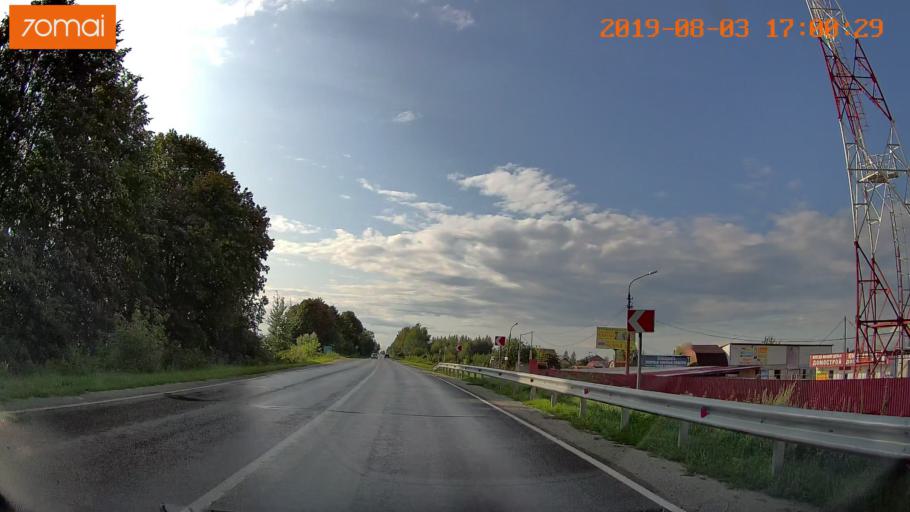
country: RU
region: Moskovskaya
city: Voskresensk
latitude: 55.3375
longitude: 38.6171
